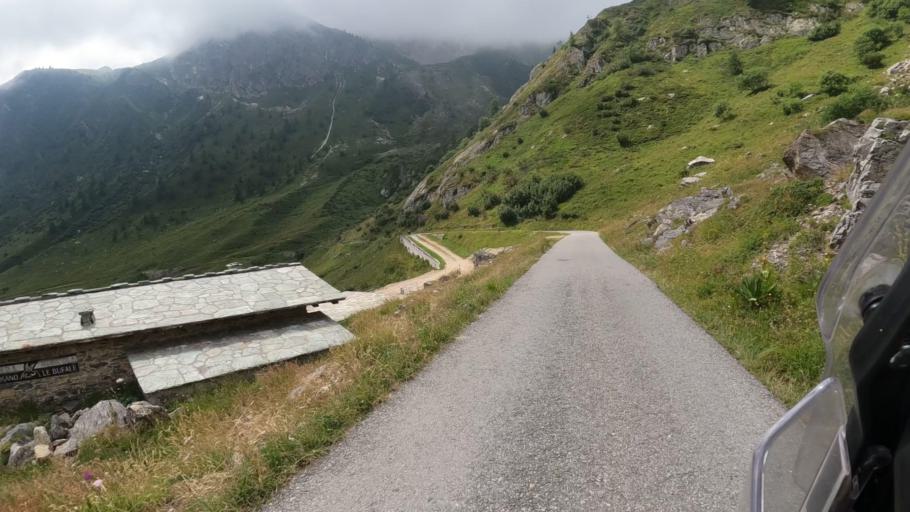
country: IT
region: Piedmont
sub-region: Provincia di Cuneo
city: Campomolino
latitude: 44.3924
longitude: 7.1487
